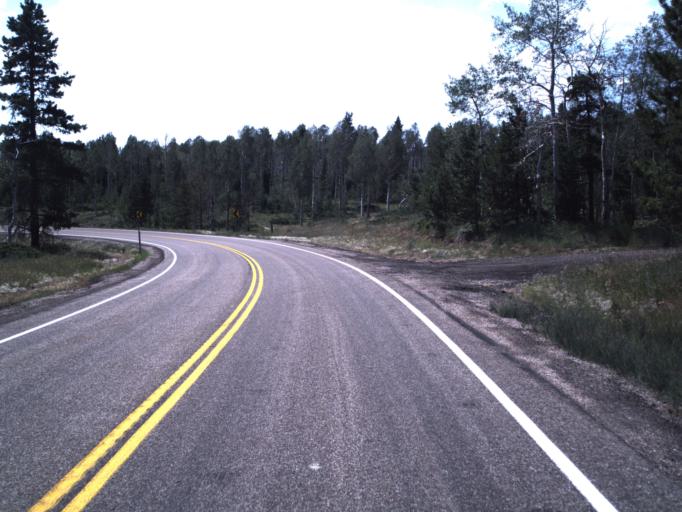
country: US
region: Utah
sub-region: Uintah County
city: Maeser
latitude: 40.7306
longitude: -109.4710
